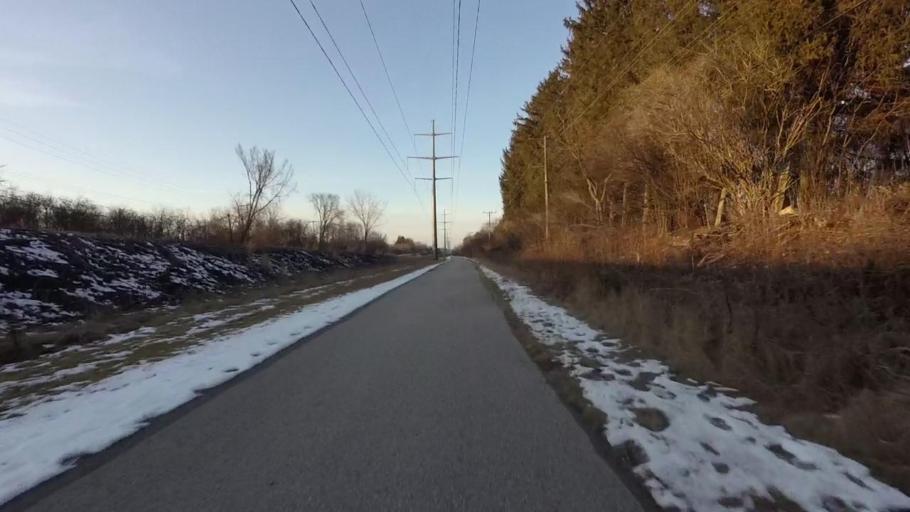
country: US
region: Wisconsin
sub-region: Milwaukee County
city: Brown Deer
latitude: 43.1667
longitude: -87.9624
